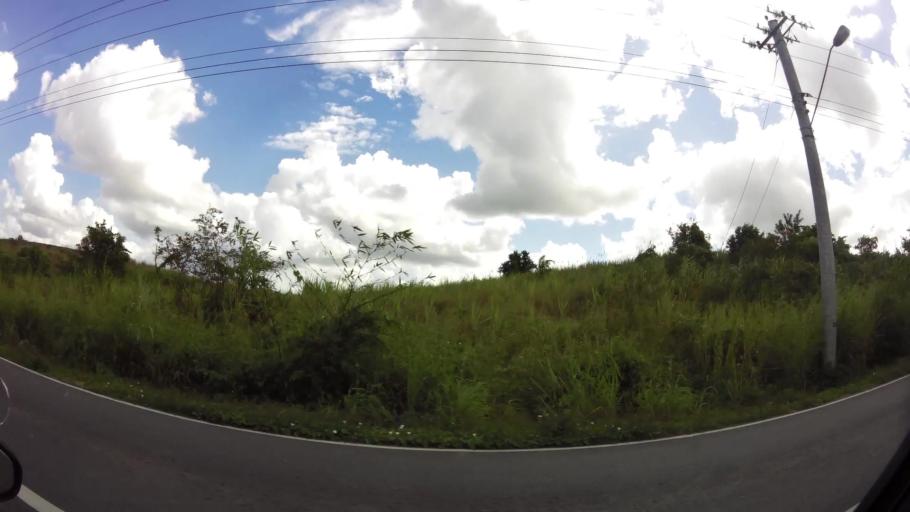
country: TT
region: Penal/Debe
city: Debe
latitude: 10.2310
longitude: -61.4839
